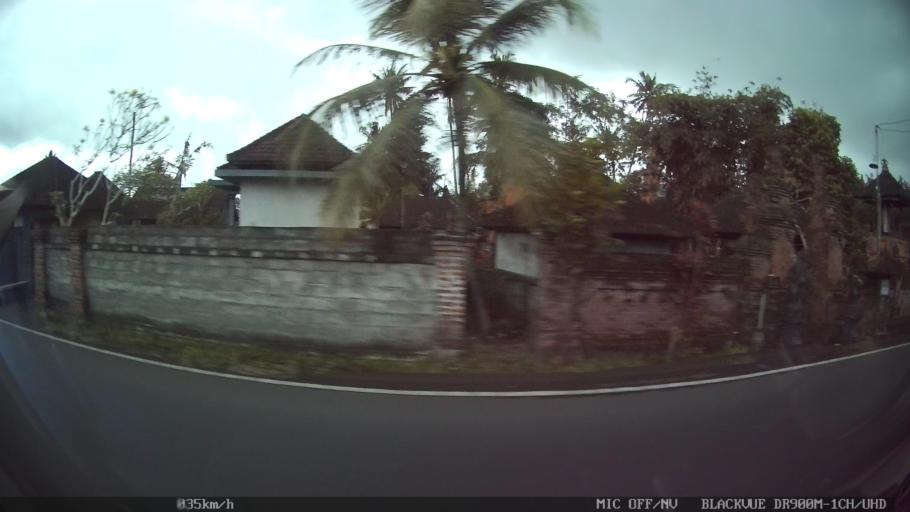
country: ID
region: Bali
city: Banjar Keraman
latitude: -8.5311
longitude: 115.2259
